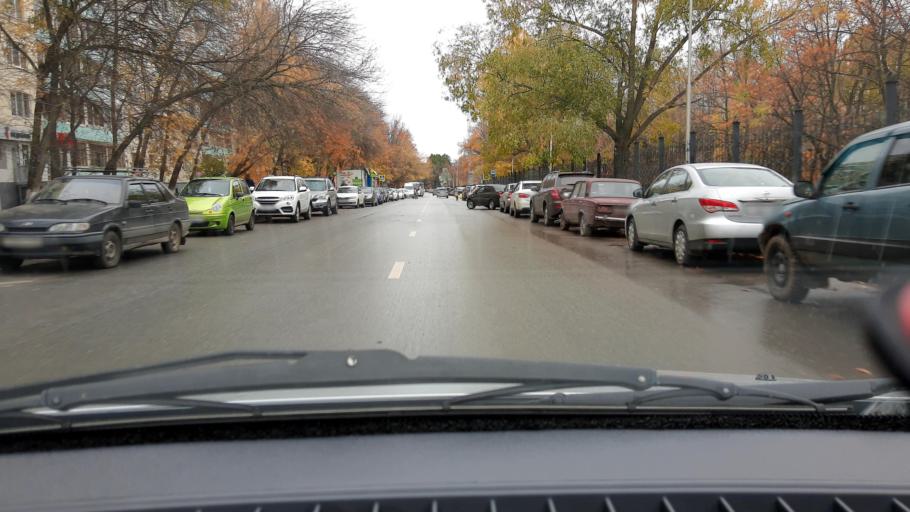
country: RU
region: Bashkortostan
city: Ufa
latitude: 54.7404
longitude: 56.0187
